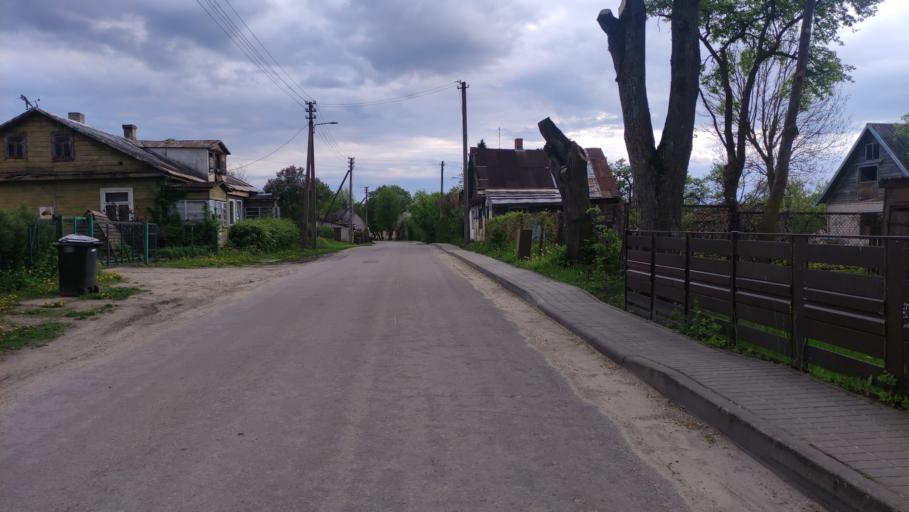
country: LT
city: Jieznas
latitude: 54.5024
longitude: 24.2538
